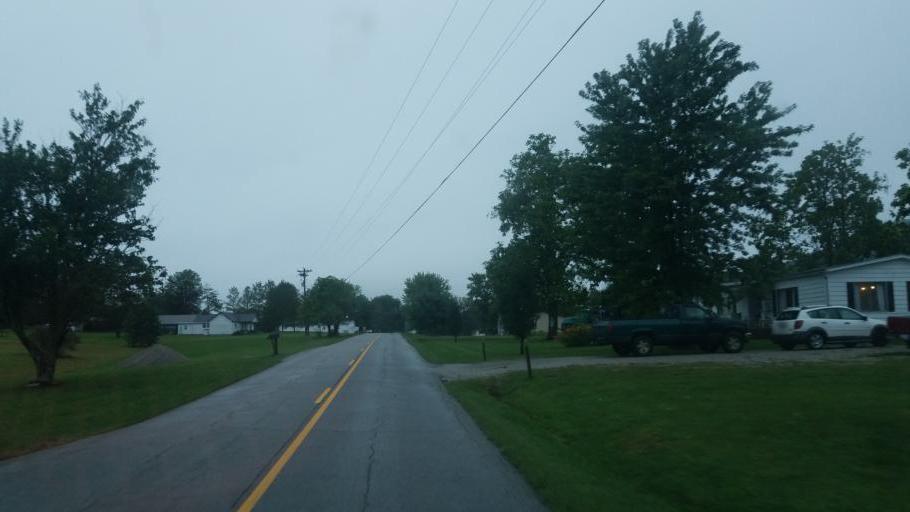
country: US
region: Kentucky
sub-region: Fleming County
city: Flemingsburg
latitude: 38.4032
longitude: -83.6252
